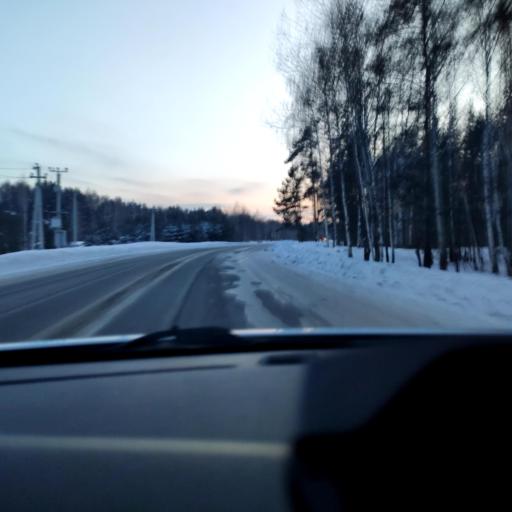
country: RU
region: Tatarstan
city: Vysokaya Gora
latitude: 55.8999
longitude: 49.2625
